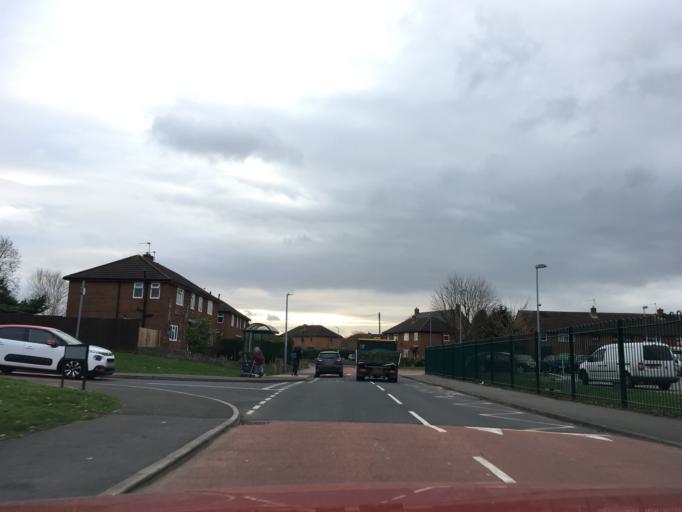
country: GB
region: Wales
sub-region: Monmouthshire
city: Caldicot
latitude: 51.5920
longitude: -2.7583
